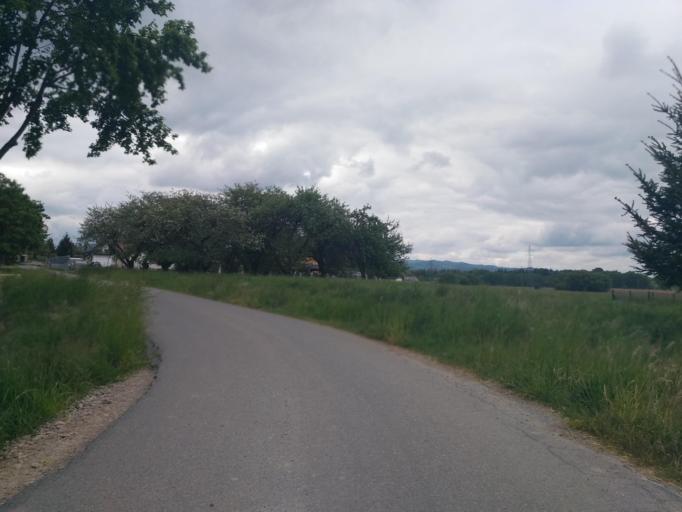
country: PL
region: Subcarpathian Voivodeship
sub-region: Powiat krosnienski
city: Jedlicze
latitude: 49.7193
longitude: 21.6905
